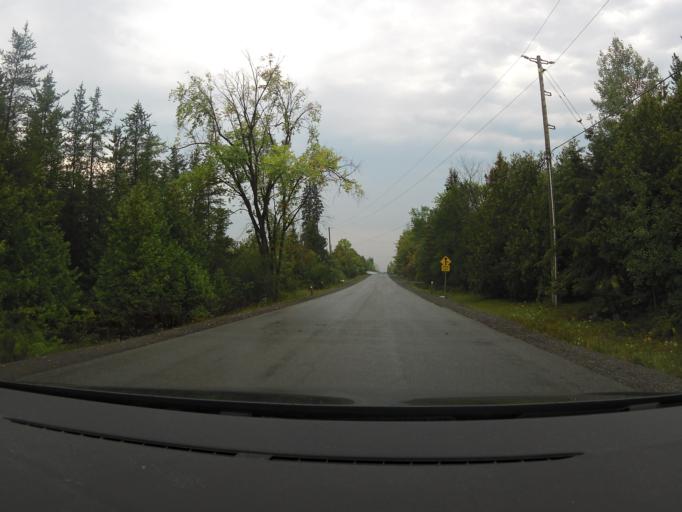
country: CA
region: Ontario
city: Carleton Place
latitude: 45.2010
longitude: -76.0599
